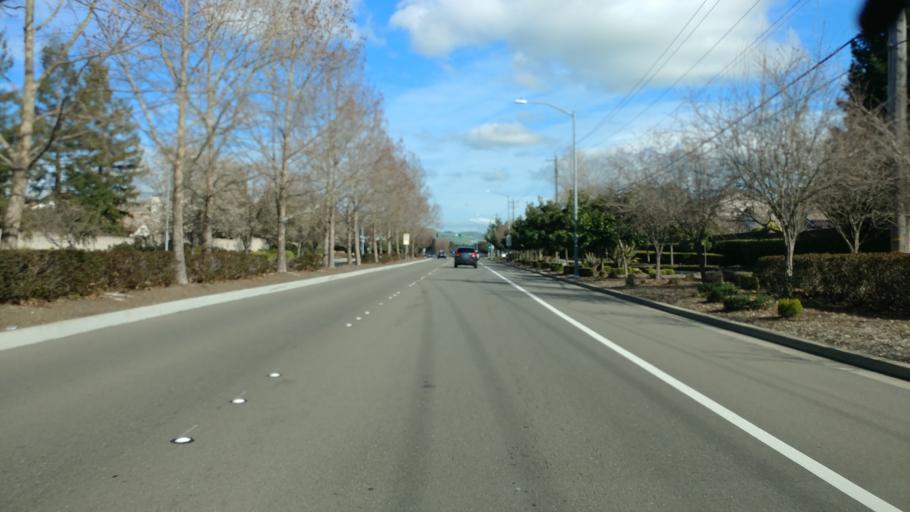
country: US
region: California
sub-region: Contra Costa County
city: Blackhawk
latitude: 37.7996
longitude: -121.9011
